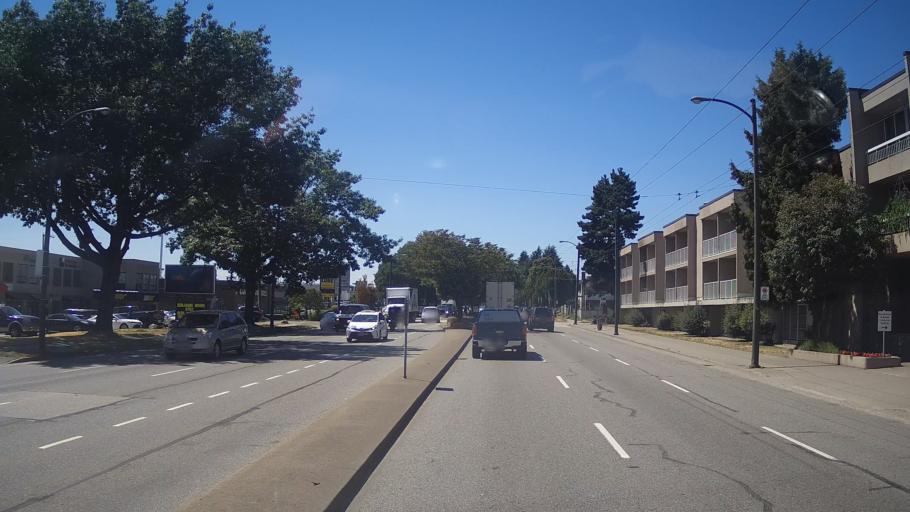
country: CA
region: British Columbia
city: Vancouver
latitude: 49.2111
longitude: -123.0918
